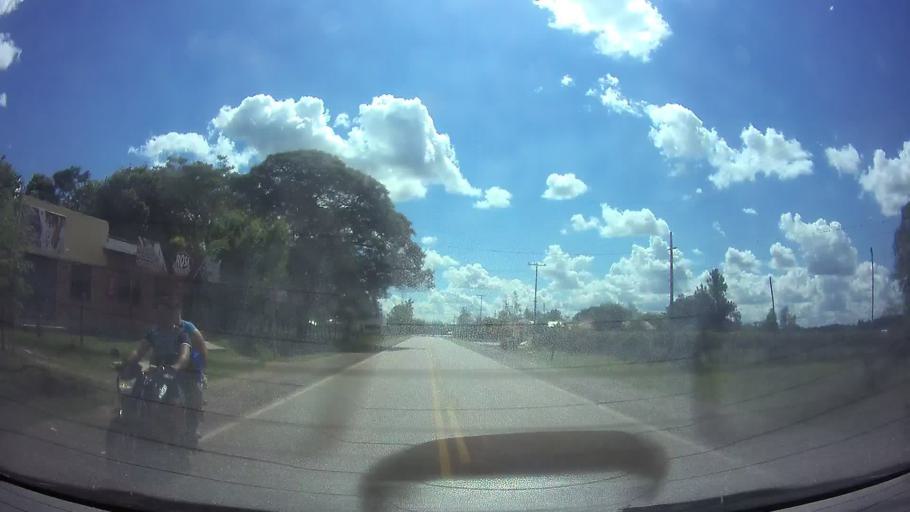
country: PY
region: Guaira
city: Itape
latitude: -25.9167
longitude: -56.6892
